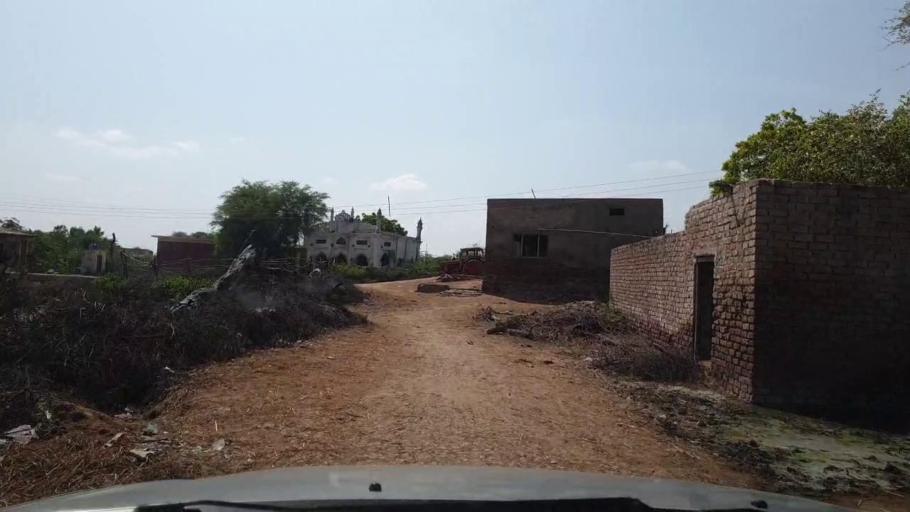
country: PK
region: Sindh
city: Rajo Khanani
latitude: 25.0348
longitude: 68.7735
